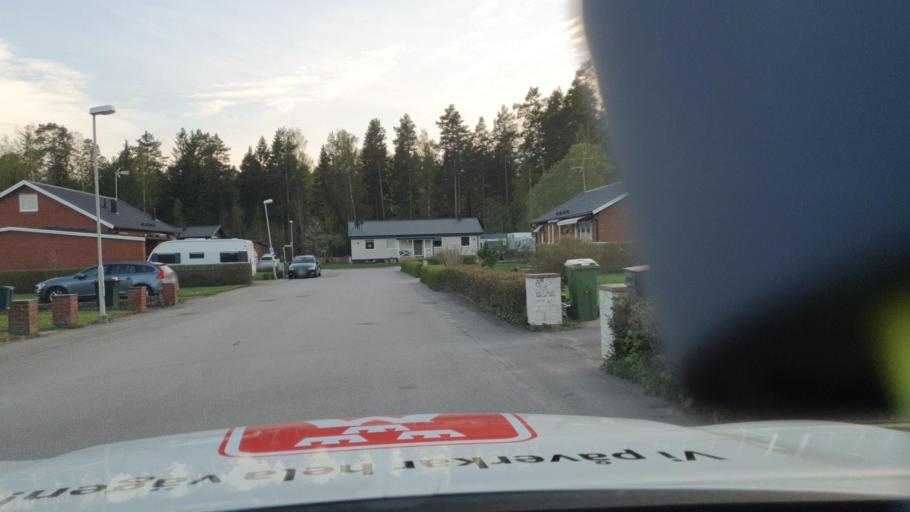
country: SE
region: OEstergoetland
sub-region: Linkopings Kommun
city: Vikingstad
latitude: 58.3856
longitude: 15.4211
